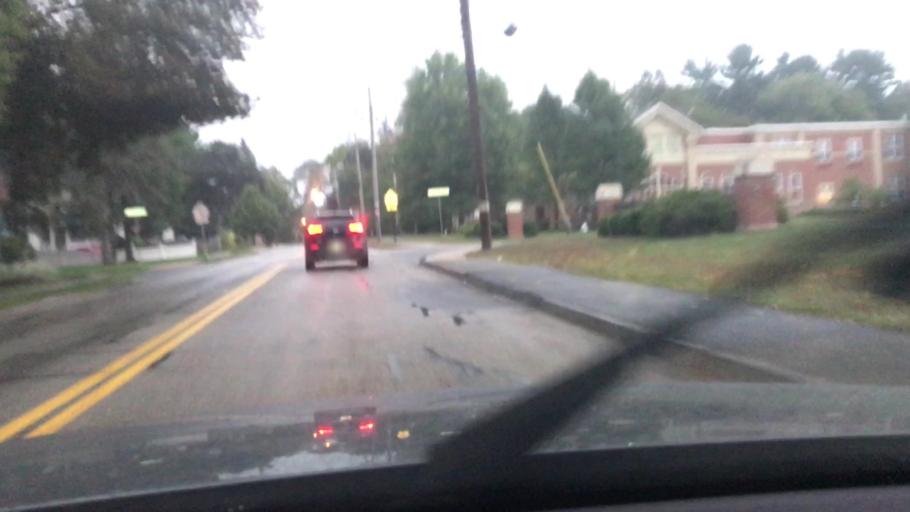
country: US
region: Massachusetts
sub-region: Essex County
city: Lynnfield
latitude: 42.5379
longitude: -71.0531
